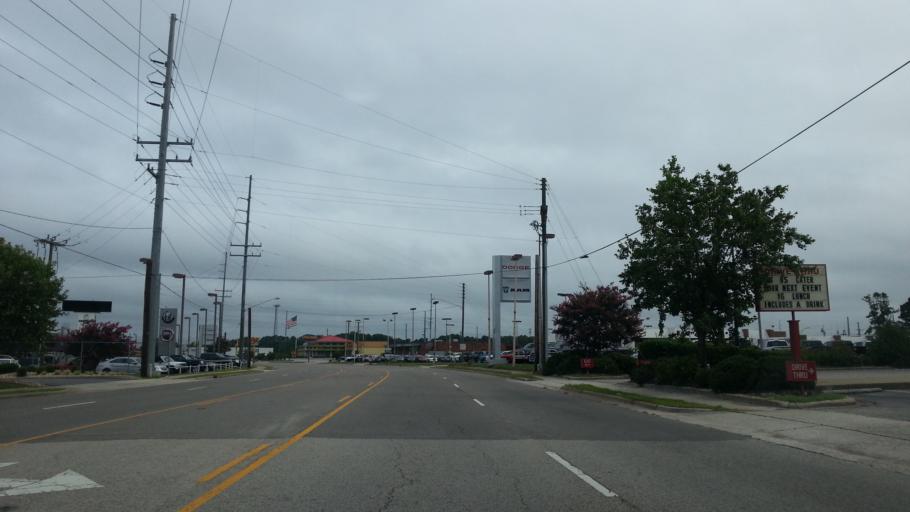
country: US
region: North Carolina
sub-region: Cumberland County
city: Fayetteville
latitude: 35.0771
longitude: -78.9546
